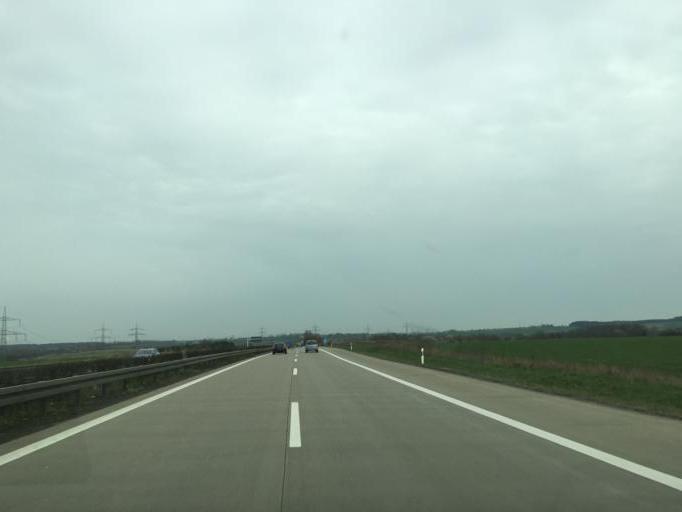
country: DE
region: Mecklenburg-Vorpommern
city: Roggentin
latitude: 54.0435
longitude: 12.1990
